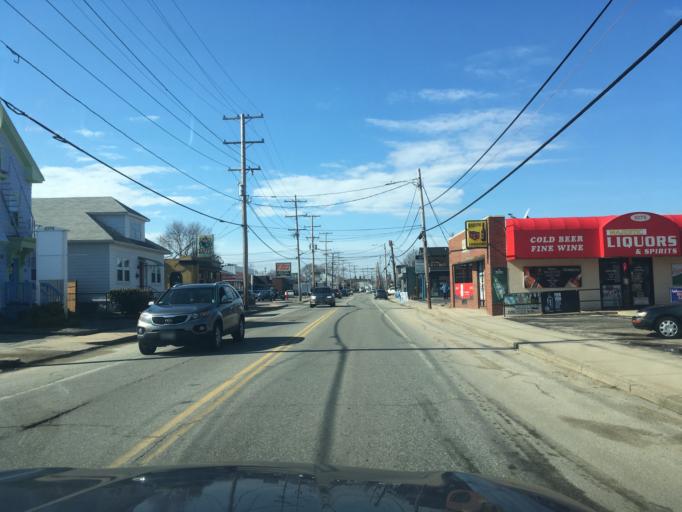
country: US
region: Rhode Island
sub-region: Providence County
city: Cranston
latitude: 41.7824
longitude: -71.4451
